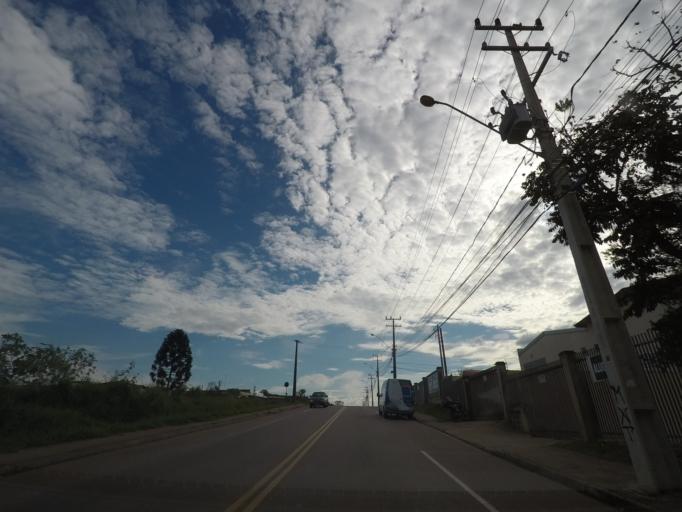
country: BR
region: Parana
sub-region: Araucaria
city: Araucaria
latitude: -25.6410
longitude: -49.3095
